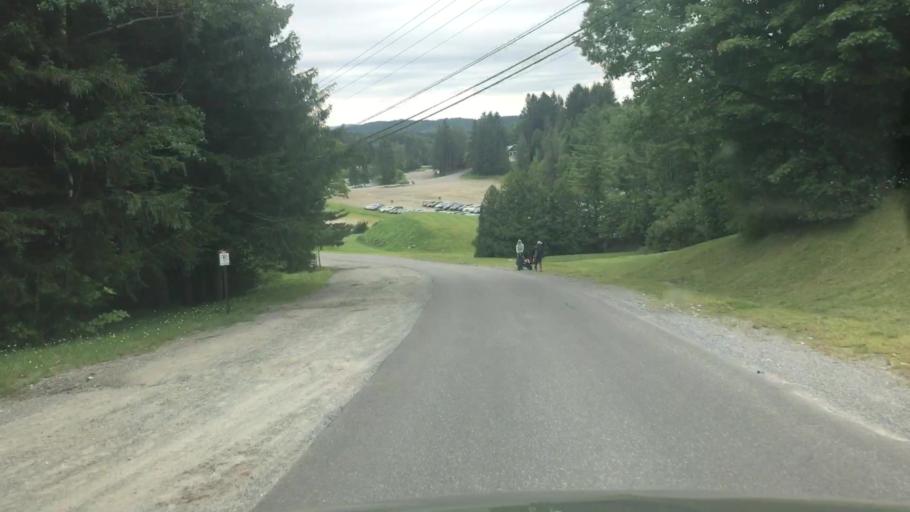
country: US
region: Vermont
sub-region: Windham County
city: Dover
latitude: 42.9682
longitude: -72.8930
